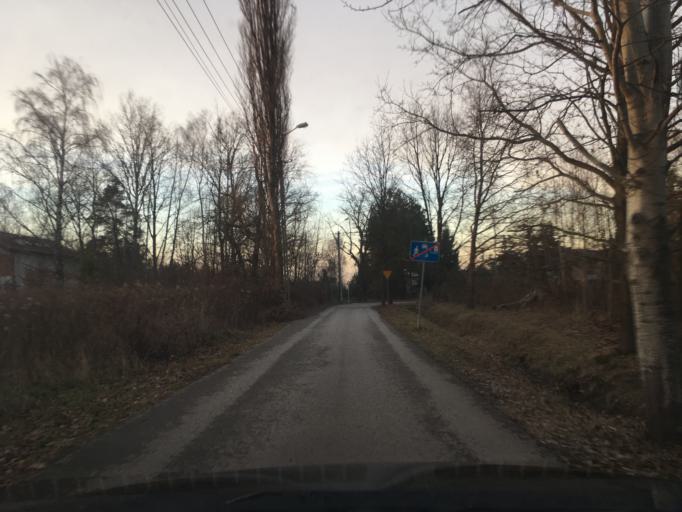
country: PL
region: Masovian Voivodeship
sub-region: Powiat piaseczynski
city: Lesznowola
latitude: 52.0403
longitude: 20.9603
